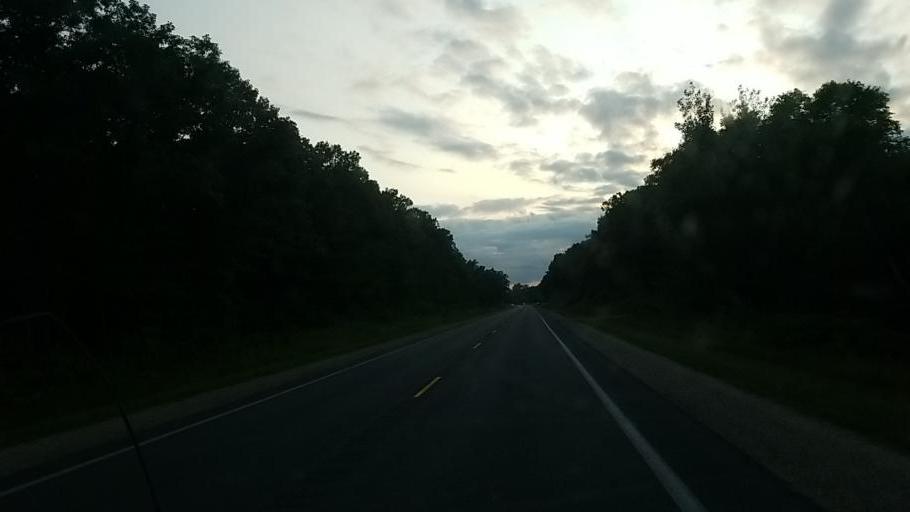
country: US
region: Michigan
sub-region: Newaygo County
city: Newaygo
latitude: 43.4050
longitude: -85.7658
